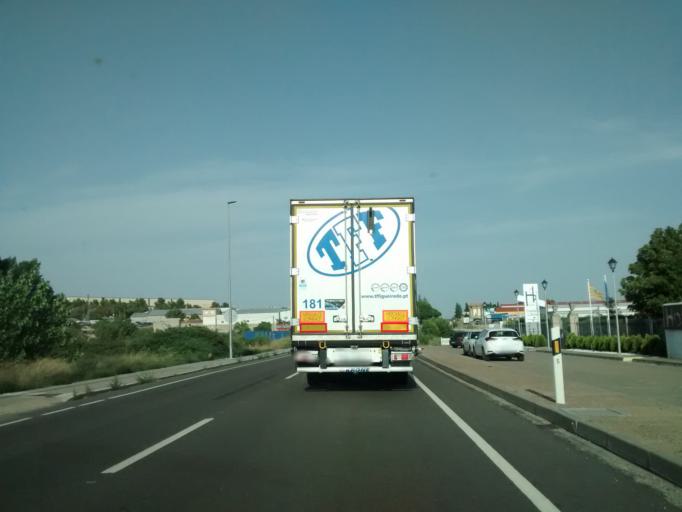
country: ES
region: Aragon
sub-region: Provincia de Zaragoza
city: Borja
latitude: 41.8319
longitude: -1.5228
